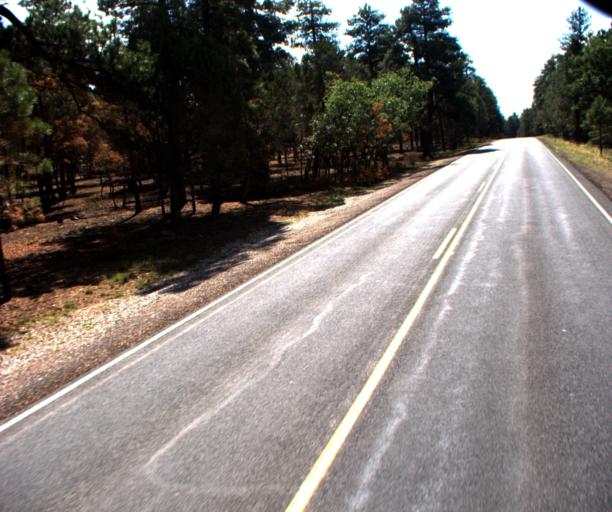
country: US
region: Arizona
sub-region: Coconino County
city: Grand Canyon
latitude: 36.0387
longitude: -112.0752
